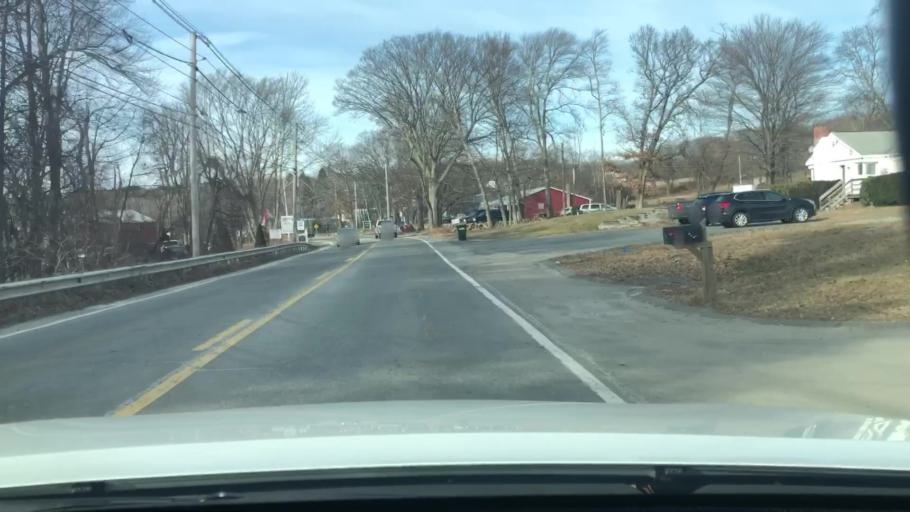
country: US
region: Massachusetts
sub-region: Worcester County
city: Upton
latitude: 42.1611
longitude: -71.5837
